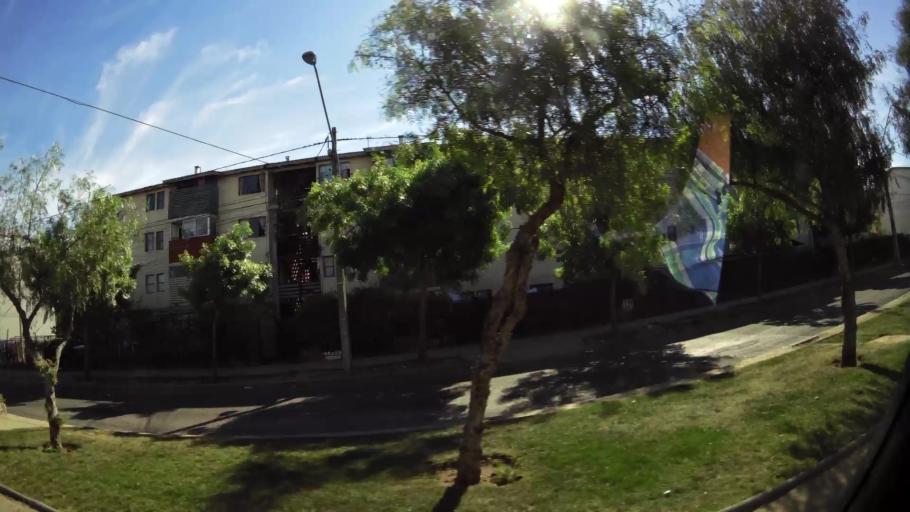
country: CL
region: Santiago Metropolitan
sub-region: Provincia de Santiago
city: Lo Prado
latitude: -33.4973
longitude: -70.7369
